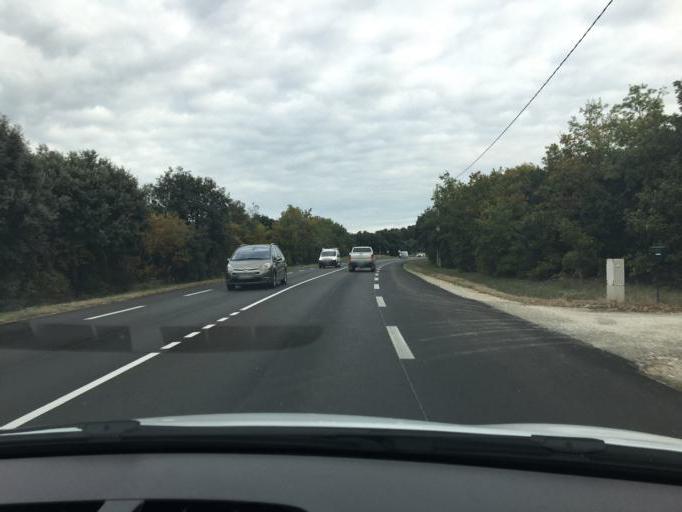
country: FR
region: Provence-Alpes-Cote d'Azur
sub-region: Departement du Vaucluse
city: Visan
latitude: 44.3403
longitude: 4.9488
